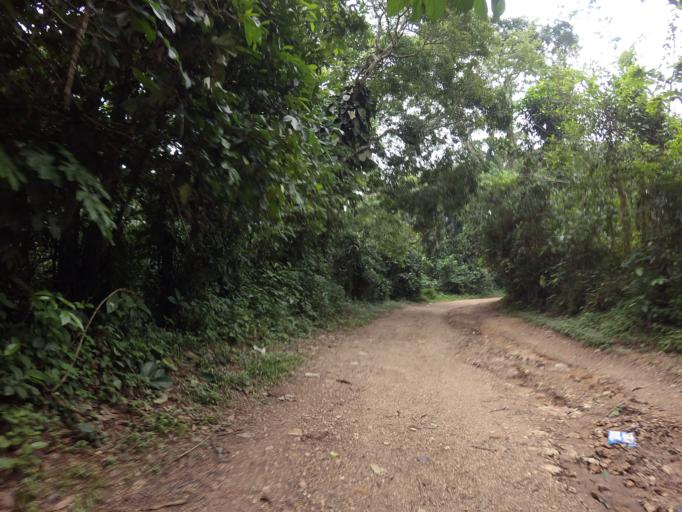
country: TG
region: Plateaux
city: Kpalime
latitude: 6.8439
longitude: 0.4410
